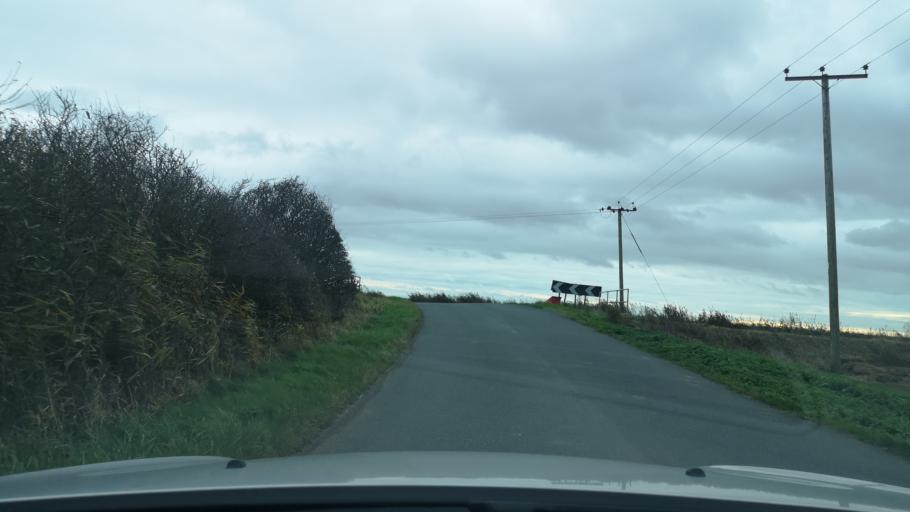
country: GB
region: England
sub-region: East Riding of Yorkshire
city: Easington
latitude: 53.6295
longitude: 0.1231
